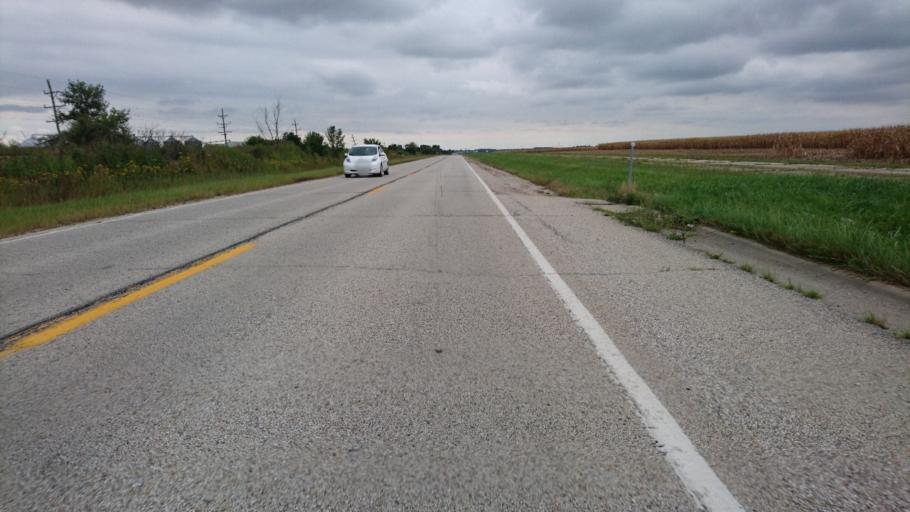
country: US
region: Illinois
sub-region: Livingston County
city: Pontiac
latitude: 40.9308
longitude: -88.5930
